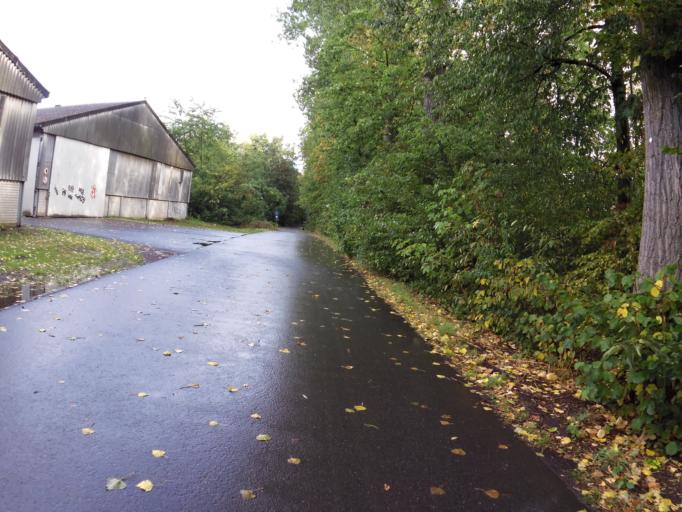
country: DE
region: Lower Saxony
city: Nienburg
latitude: 52.6452
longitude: 9.2034
